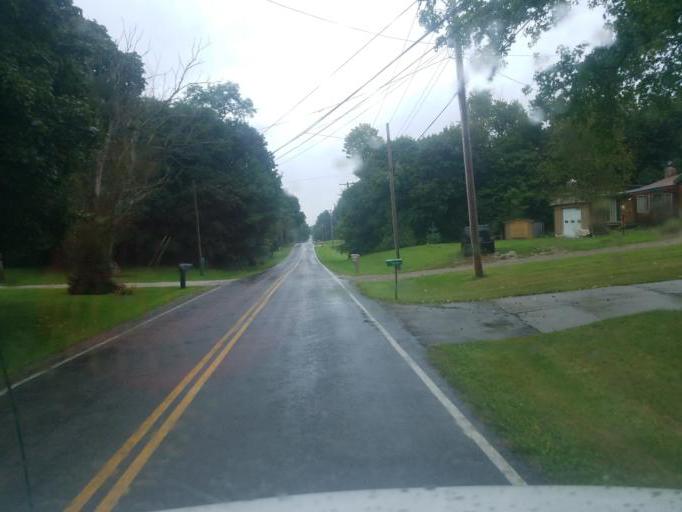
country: US
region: Ohio
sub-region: Medina County
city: Seville
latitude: 41.0100
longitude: -81.8455
